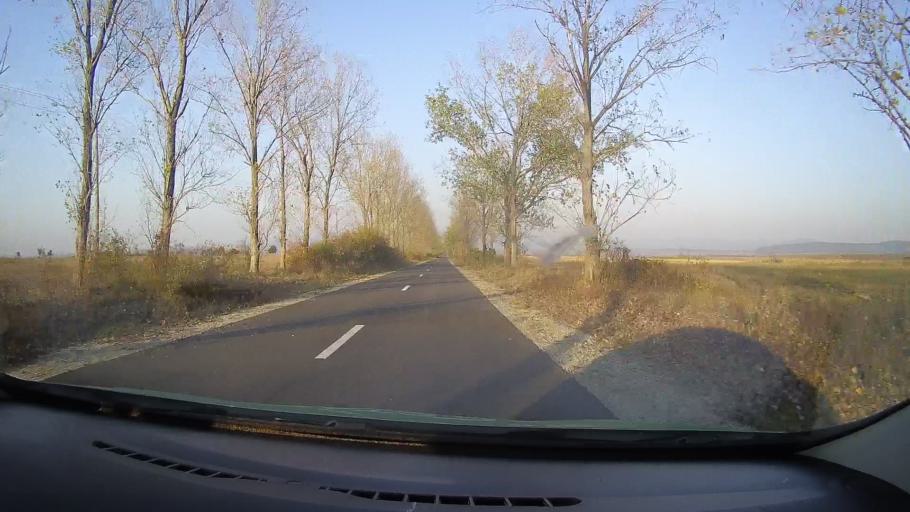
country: RO
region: Arad
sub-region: Comuna Barsa
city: Barsa
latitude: 46.3654
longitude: 22.0379
